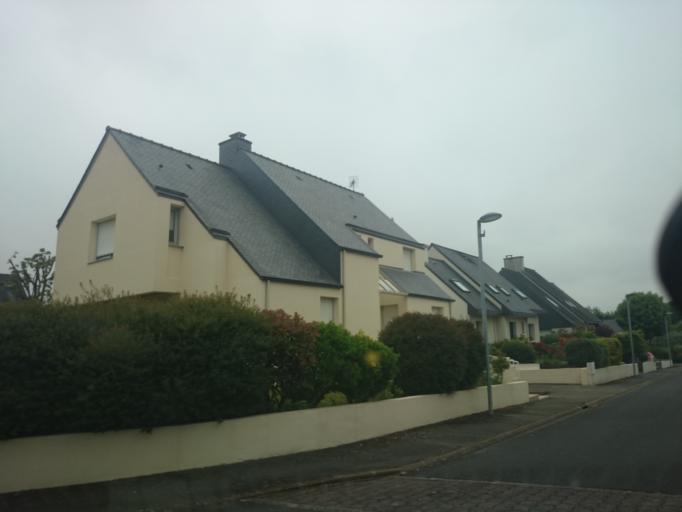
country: FR
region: Brittany
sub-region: Departement d'Ille-et-Vilaine
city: Cesson-Sevigne
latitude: 48.1272
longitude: -1.6038
